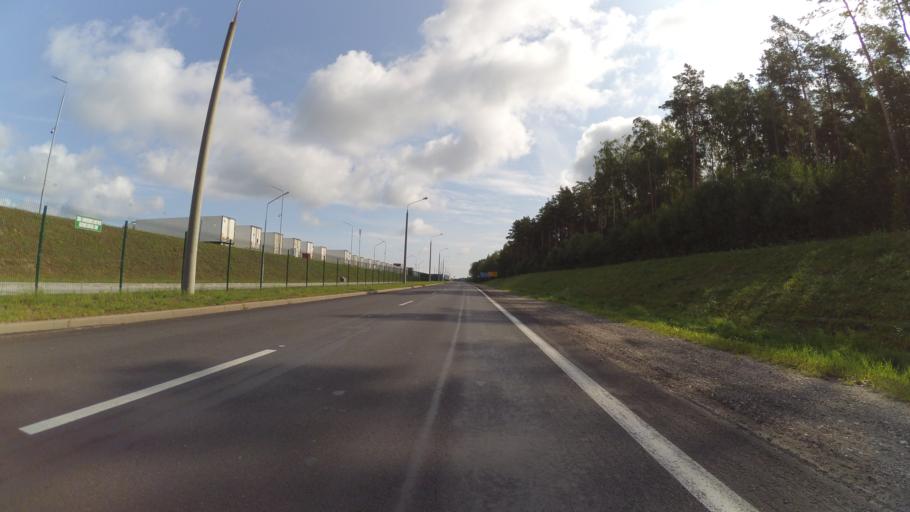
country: PL
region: Podlasie
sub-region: Powiat sokolski
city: Kuznica
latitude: 53.5251
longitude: 23.6721
